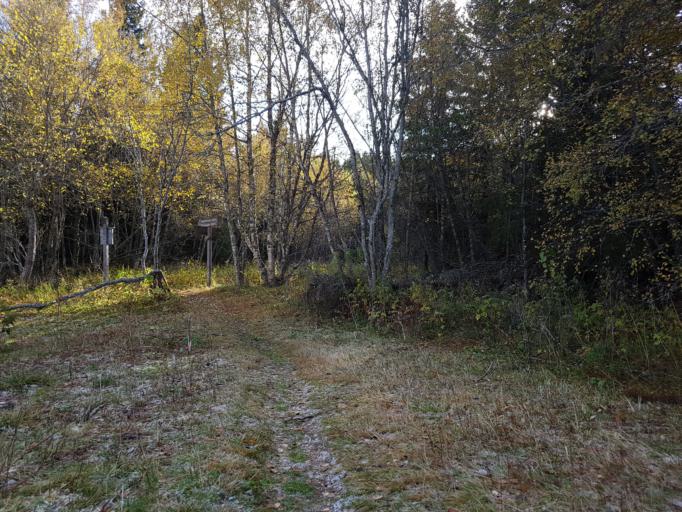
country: NO
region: Sor-Trondelag
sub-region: Trondheim
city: Trondheim
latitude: 63.4462
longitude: 10.2796
